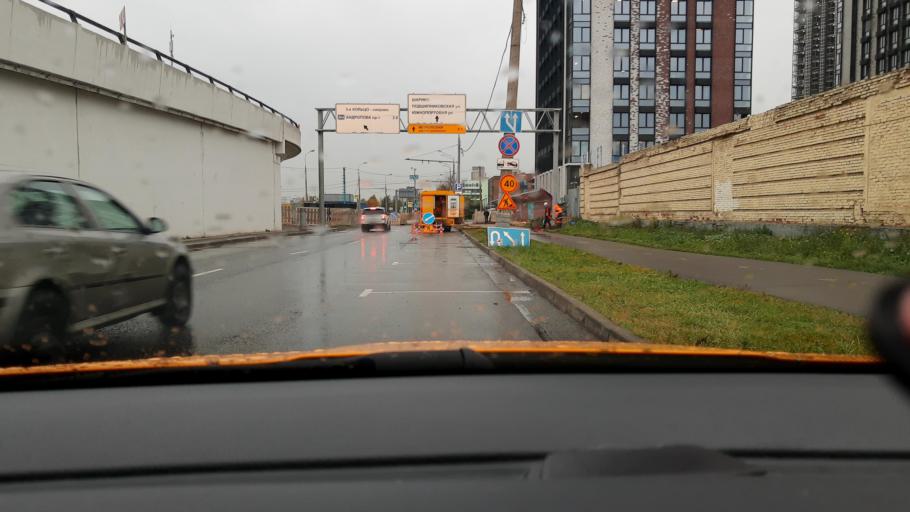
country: RU
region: Moscow
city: Taganskiy
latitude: 55.7198
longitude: 37.6960
